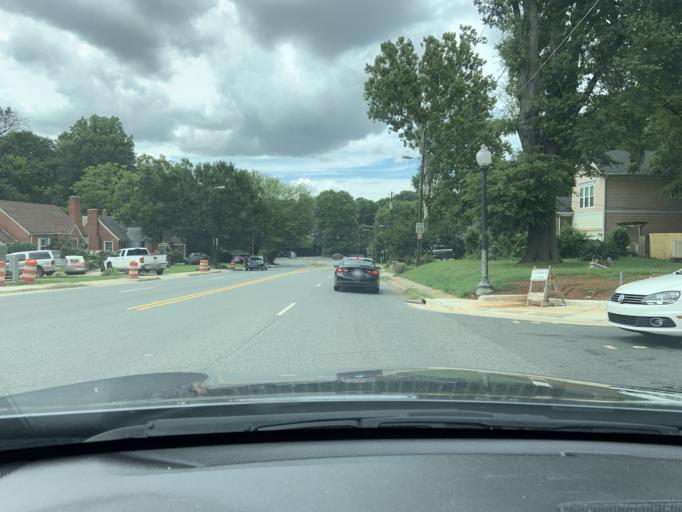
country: US
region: North Carolina
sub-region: Mecklenburg County
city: Charlotte
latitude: 35.2171
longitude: -80.8698
